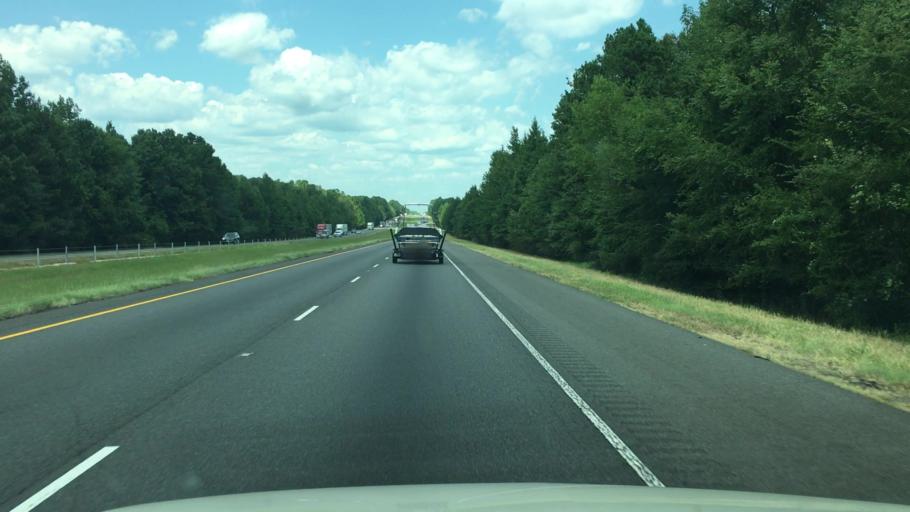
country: US
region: Arkansas
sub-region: Clark County
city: Arkadelphia
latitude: 34.0481
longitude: -93.1357
